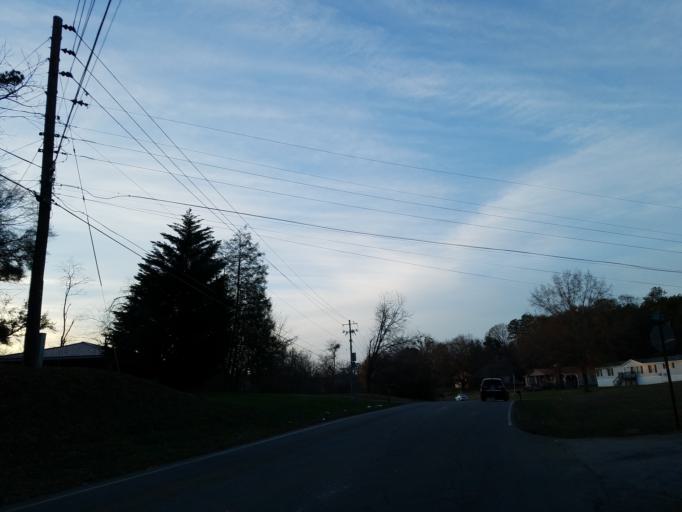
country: US
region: Georgia
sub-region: Bartow County
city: Cartersville
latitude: 34.1969
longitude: -84.8082
